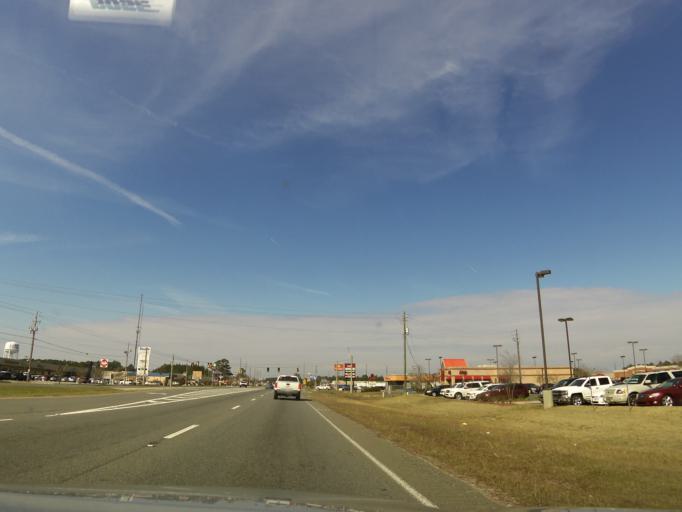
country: US
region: Georgia
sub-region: Ware County
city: Waycross
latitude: 31.1944
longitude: -82.3200
